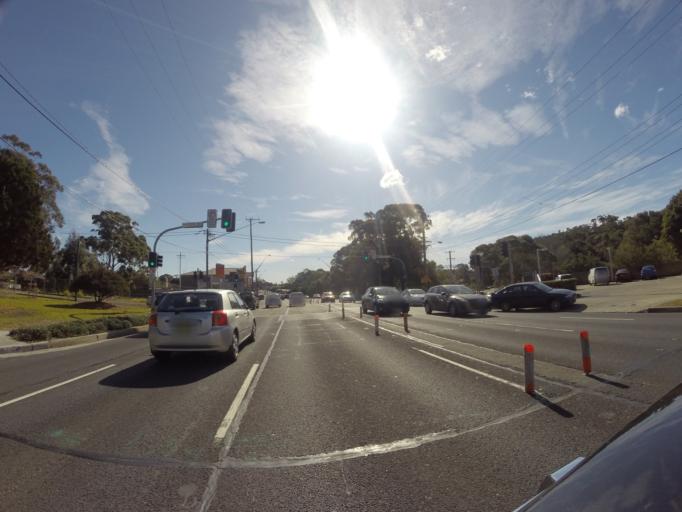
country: AU
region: New South Wales
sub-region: Kogarah
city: Blakehurst
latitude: -33.9903
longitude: 151.1133
